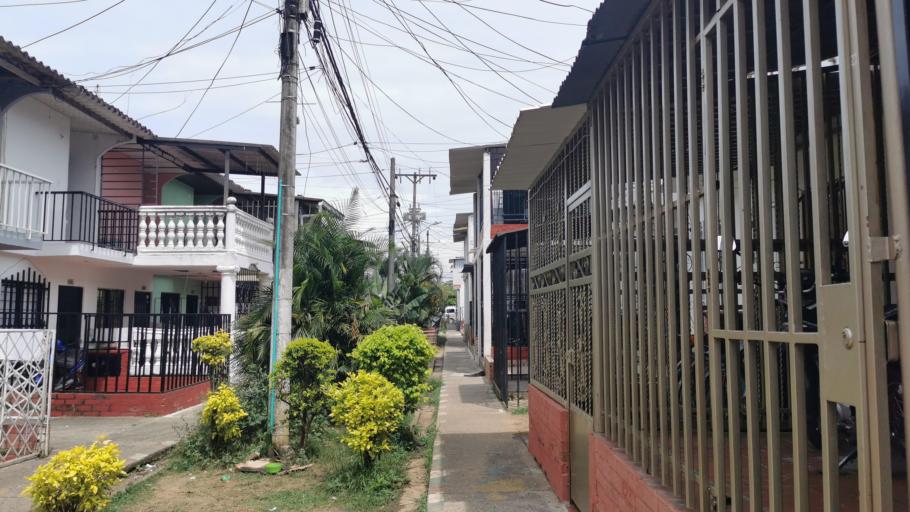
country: CO
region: Valle del Cauca
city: Jamundi
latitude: 3.2527
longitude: -76.5341
